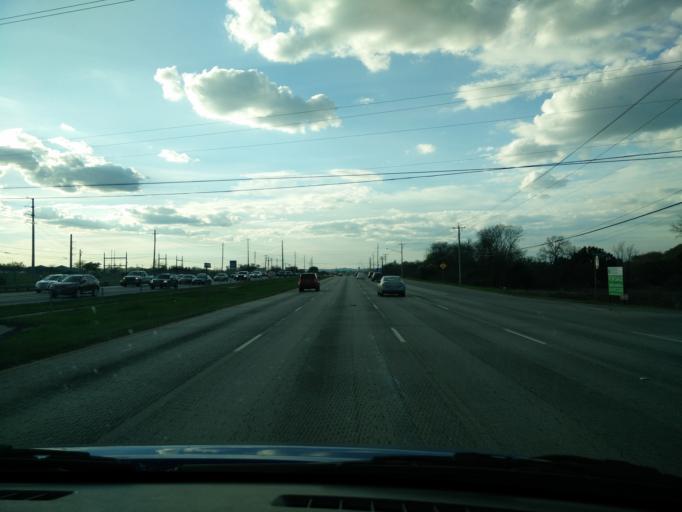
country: US
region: Texas
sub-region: Travis County
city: Austin
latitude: 30.2185
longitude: -97.6686
